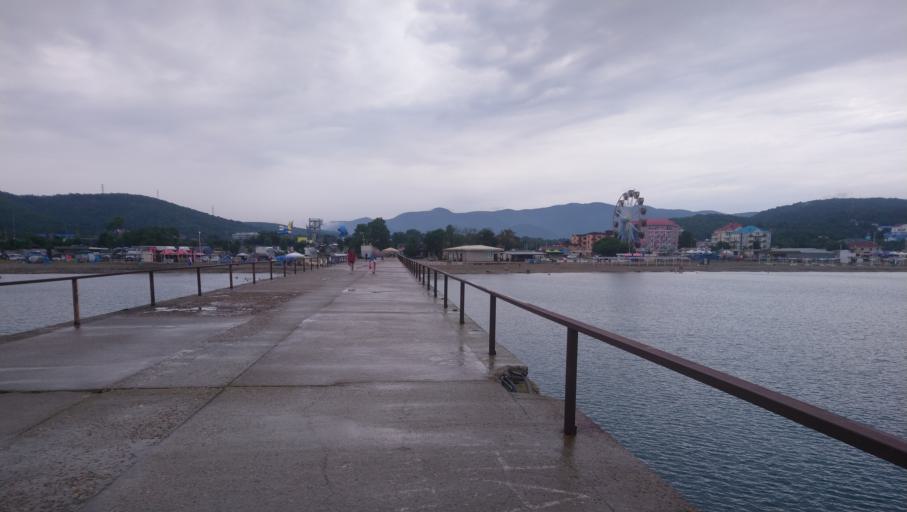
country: RU
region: Krasnodarskiy
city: Lermontovo
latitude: 44.3006
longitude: 38.7445
